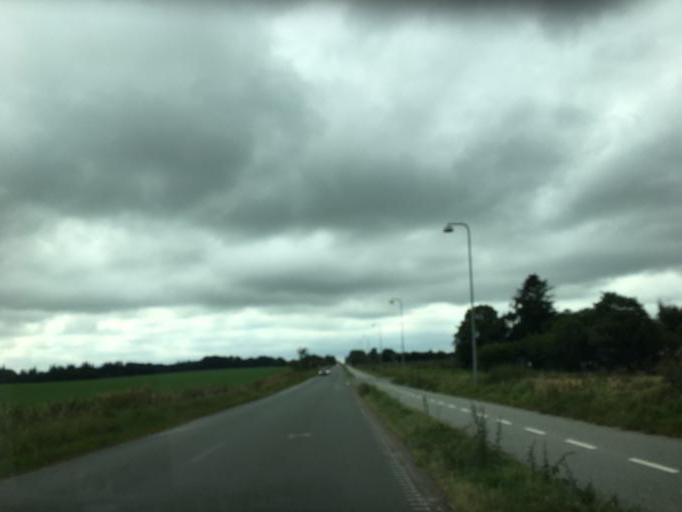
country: DK
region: South Denmark
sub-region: Kolding Kommune
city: Kolding
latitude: 55.5807
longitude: 9.4926
